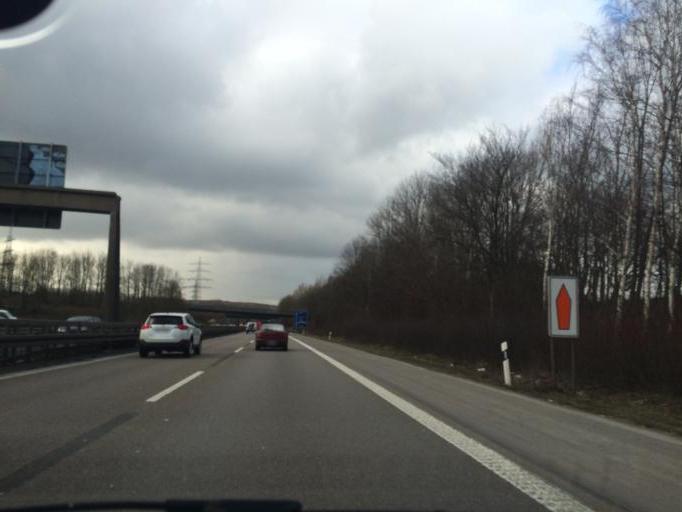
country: DE
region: North Rhine-Westphalia
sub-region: Regierungsbezirk Arnsberg
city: Bochum
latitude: 51.4712
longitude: 7.2856
